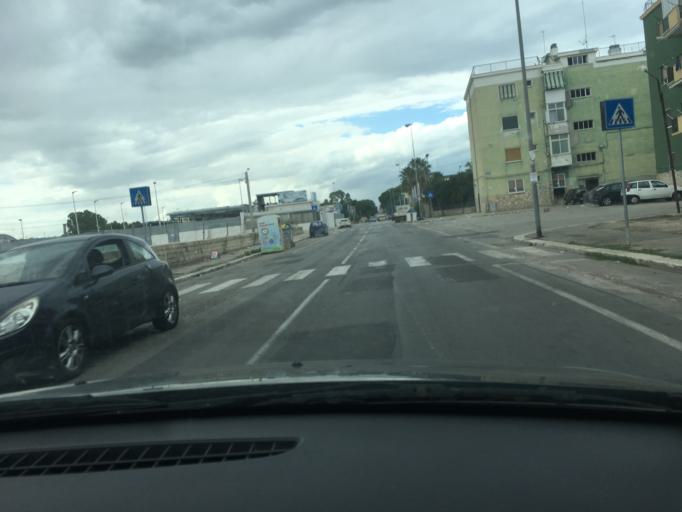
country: IT
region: Apulia
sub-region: Provincia di Bari
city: Bari
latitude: 41.1310
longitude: 16.8367
